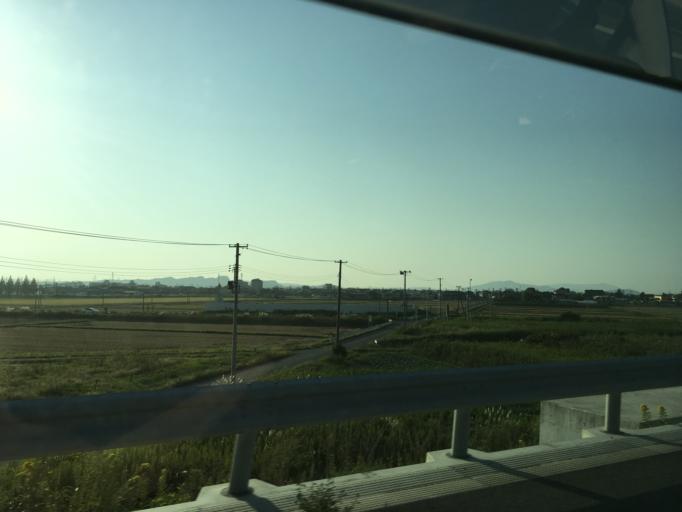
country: JP
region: Miyagi
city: Ishinomaki
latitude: 38.4842
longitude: 141.2921
